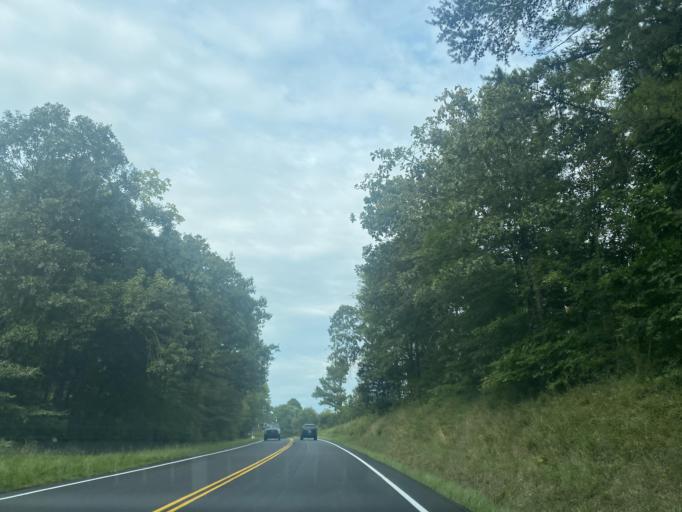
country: US
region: South Carolina
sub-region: Cherokee County
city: Blacksburg
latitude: 35.0917
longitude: -81.5601
